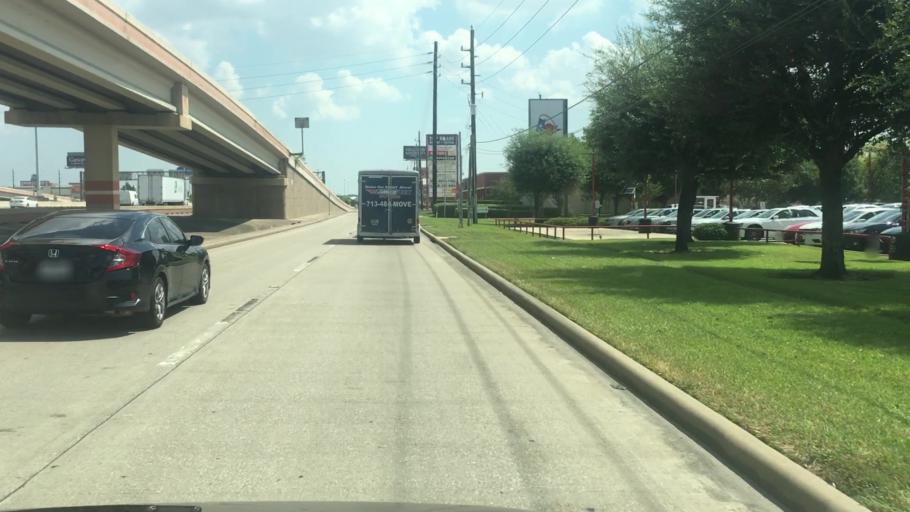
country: US
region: Texas
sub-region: Fort Bend County
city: Meadows Place
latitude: 29.6468
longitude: -95.5725
